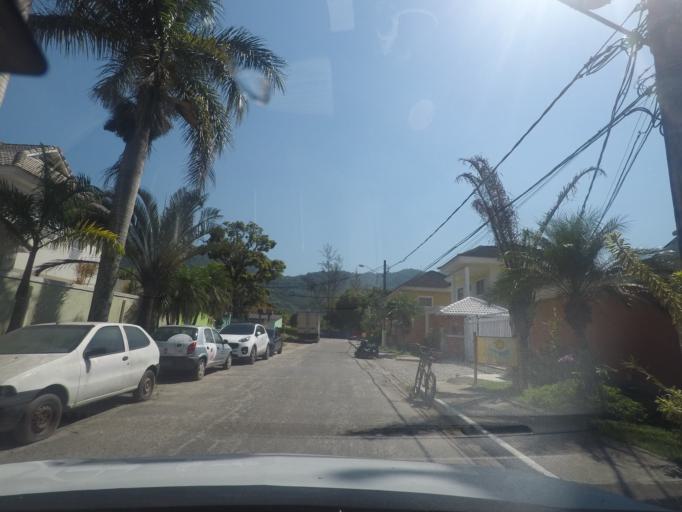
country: BR
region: Rio de Janeiro
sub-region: Nilopolis
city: Nilopolis
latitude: -22.9833
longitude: -43.4538
